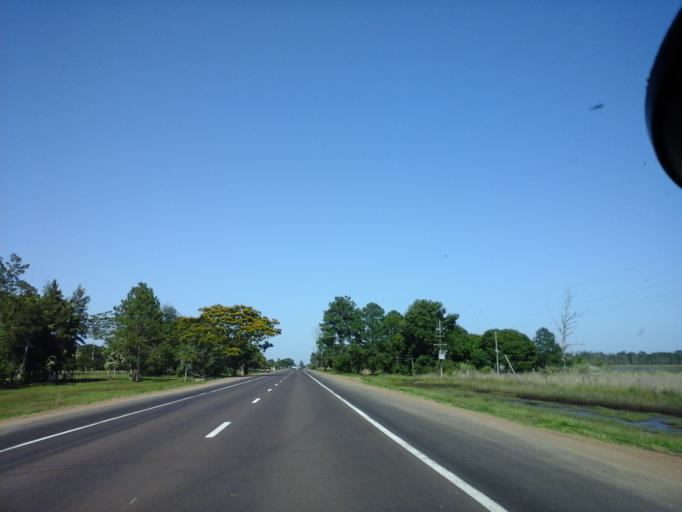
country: AR
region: Corrientes
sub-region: Departamento de Itati
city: Itati
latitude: -27.3668
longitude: -58.3425
